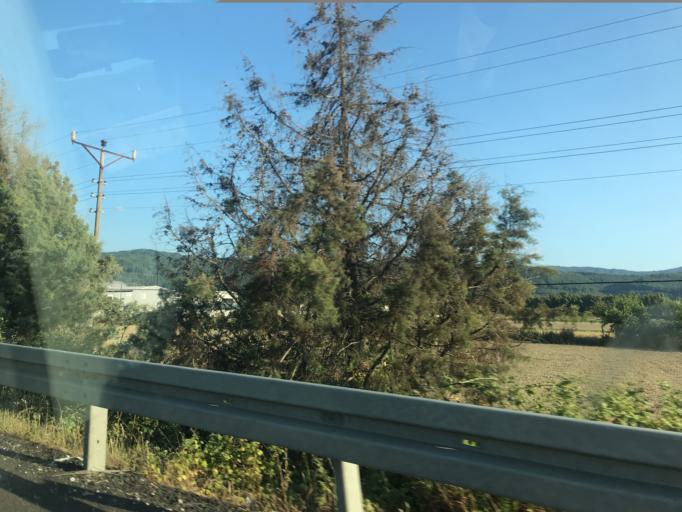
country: TR
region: Mugla
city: Ula
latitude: 37.0404
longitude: 28.3829
